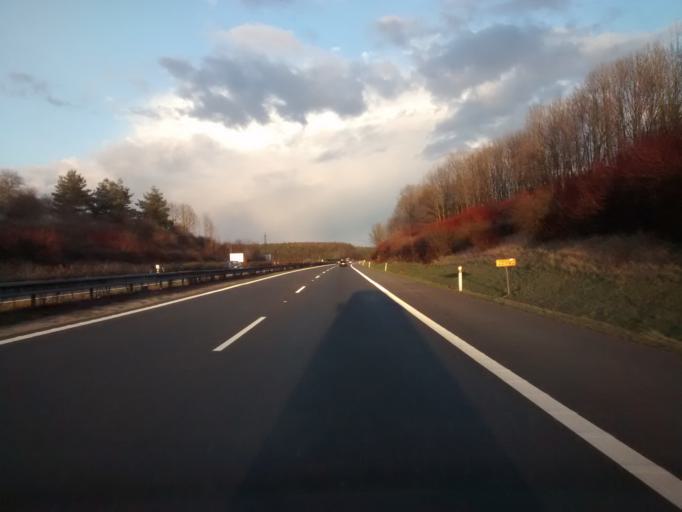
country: CZ
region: Central Bohemia
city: Poricany
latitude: 50.1283
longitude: 14.8943
